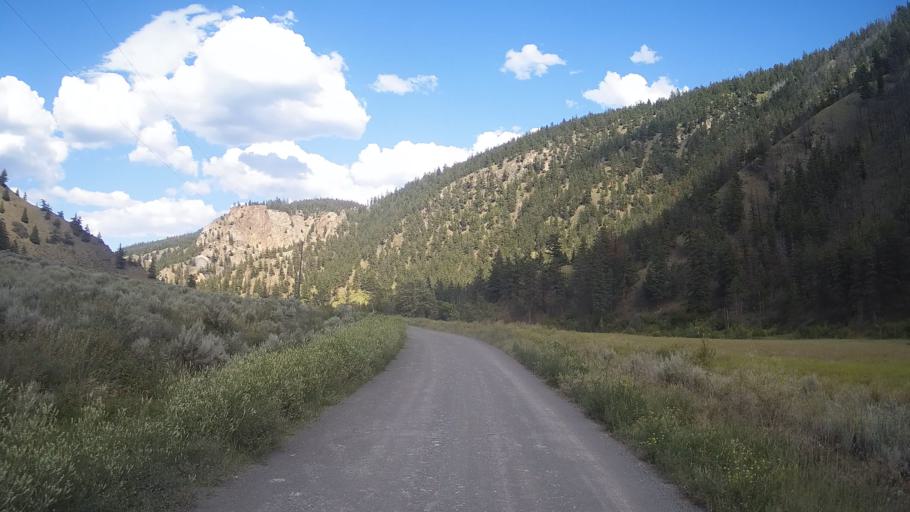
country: CA
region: British Columbia
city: Lillooet
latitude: 51.2237
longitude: -122.0698
